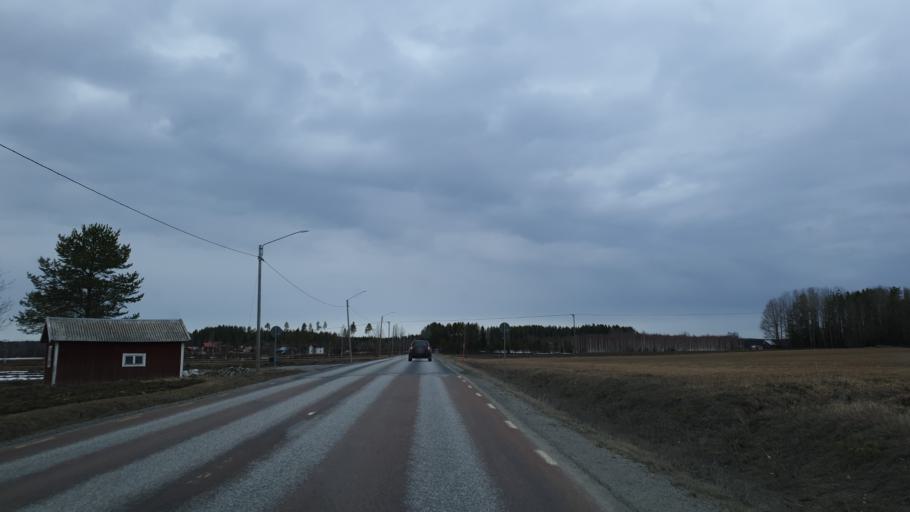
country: SE
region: Vaesterbotten
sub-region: Skelleftea Kommun
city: Viken
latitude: 64.6425
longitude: 20.9604
